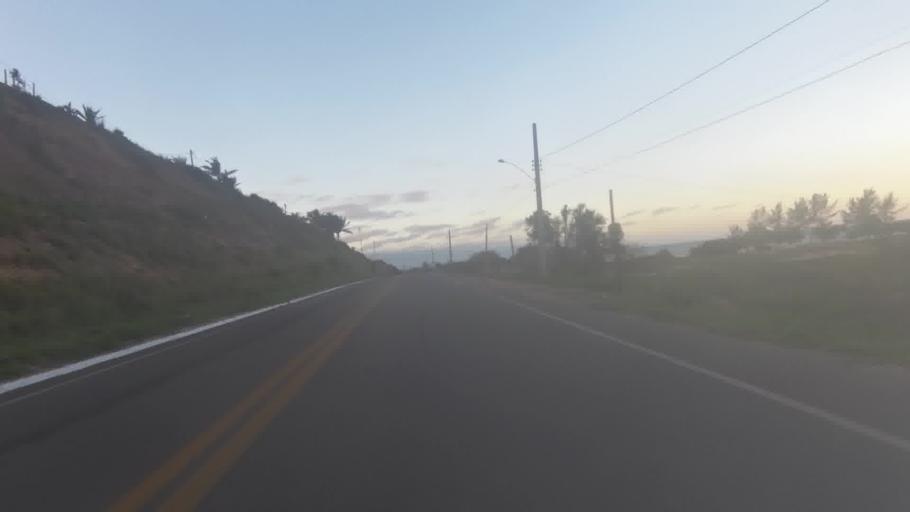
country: BR
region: Espirito Santo
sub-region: Marataizes
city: Marataizes
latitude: -21.1110
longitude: -40.8553
